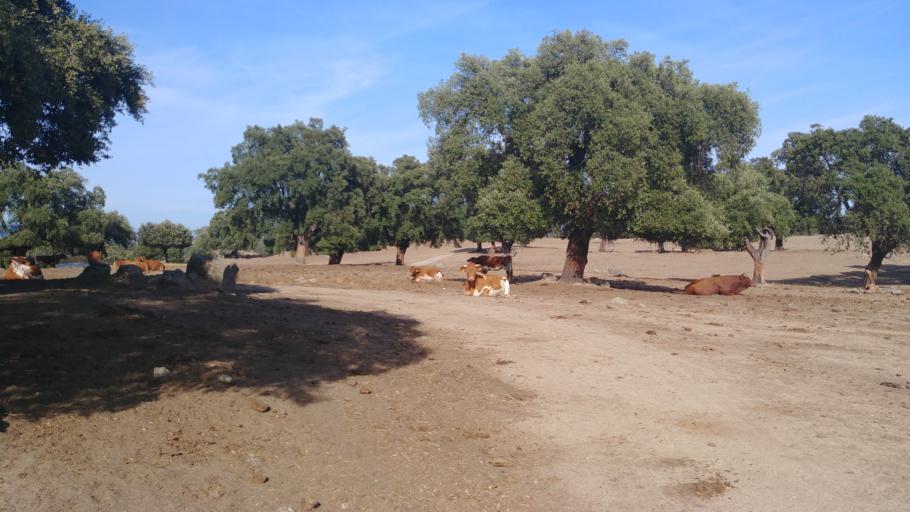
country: ES
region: Castille-La Mancha
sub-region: Province of Toledo
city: Navalcan
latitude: 40.0662
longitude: -5.1160
